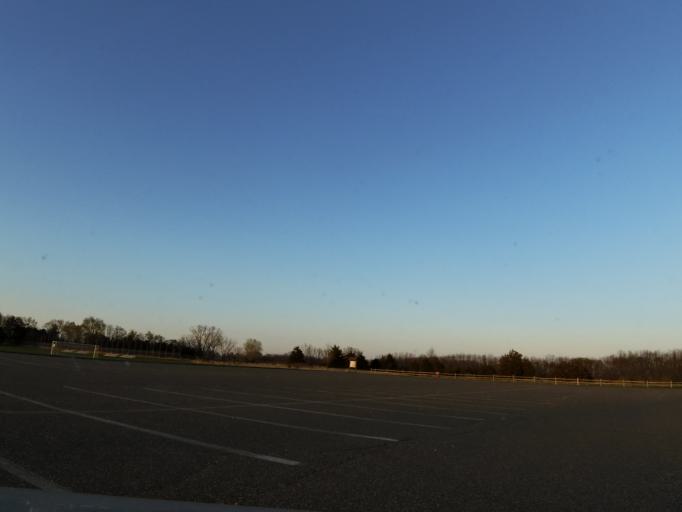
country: US
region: Minnesota
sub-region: Washington County
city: Lakeland
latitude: 44.9541
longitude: -92.7877
